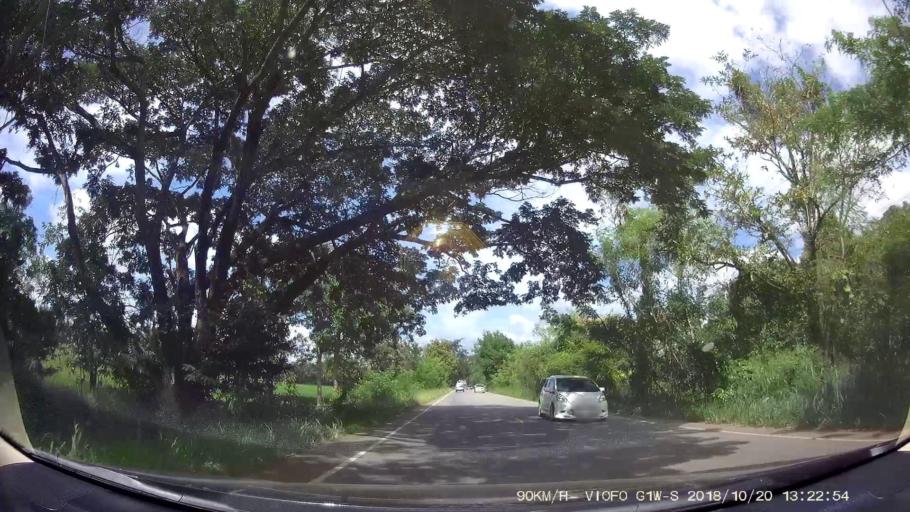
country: TH
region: Chaiyaphum
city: Khon San
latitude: 16.5773
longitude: 101.9185
